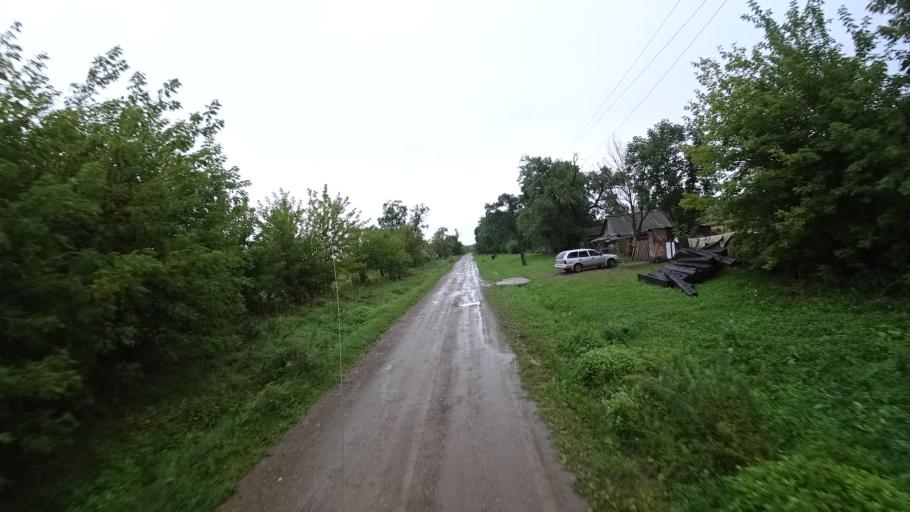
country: RU
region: Primorskiy
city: Monastyrishche
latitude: 44.2525
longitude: 132.4263
